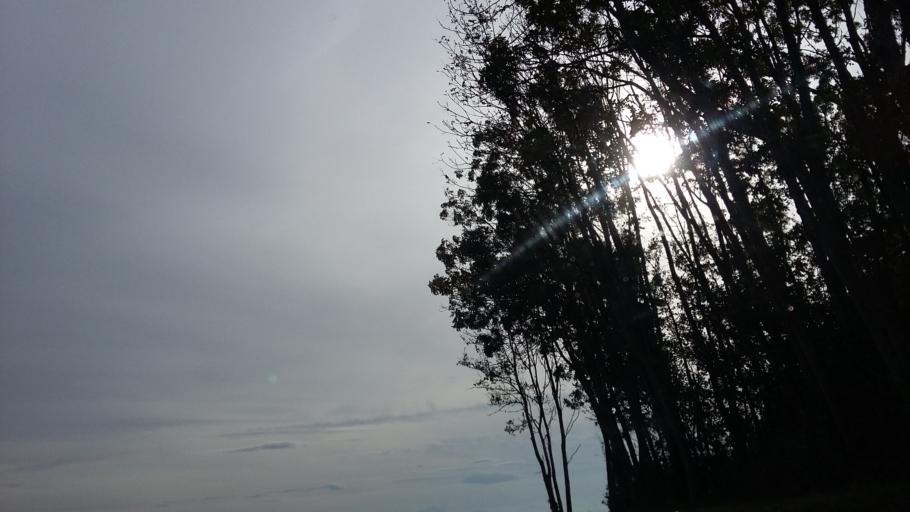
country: DE
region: Bavaria
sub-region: Upper Bavaria
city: Munsing
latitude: 47.8959
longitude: 11.3621
